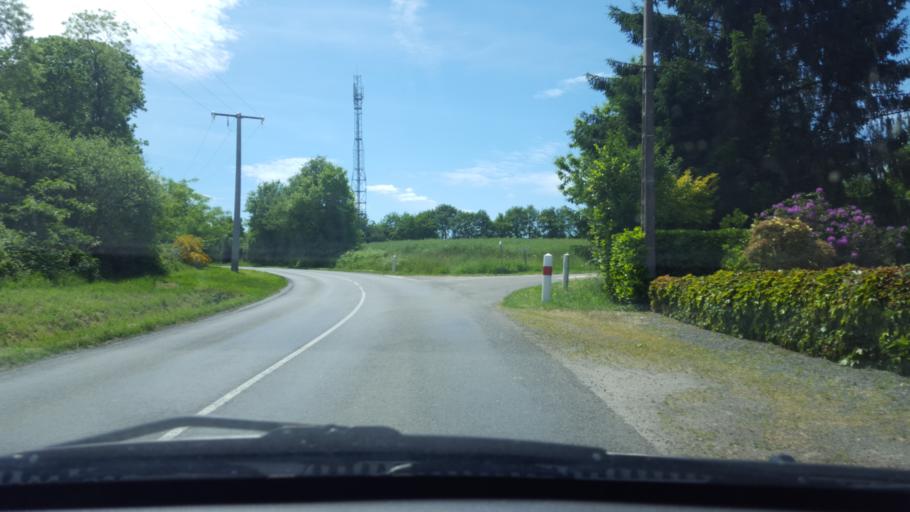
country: FR
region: Pays de la Loire
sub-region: Departement de la Loire-Atlantique
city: Saint-Philbert-de-Grand-Lieu
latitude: 47.0251
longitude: -1.6447
